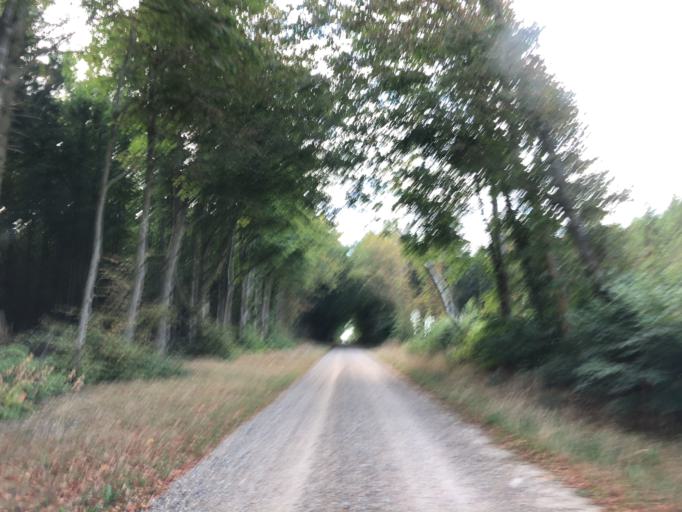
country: DK
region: Central Jutland
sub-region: Holstebro Kommune
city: Ulfborg
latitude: 56.1619
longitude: 8.4066
